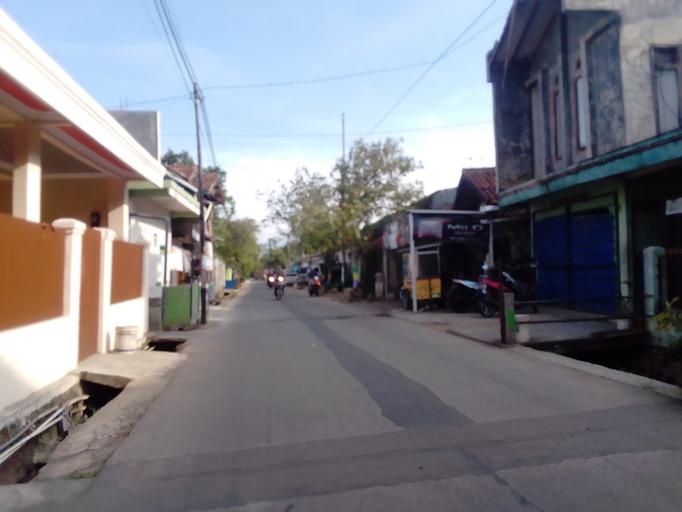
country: ID
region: West Java
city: Cileunyi
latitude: -6.9276
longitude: 107.7048
